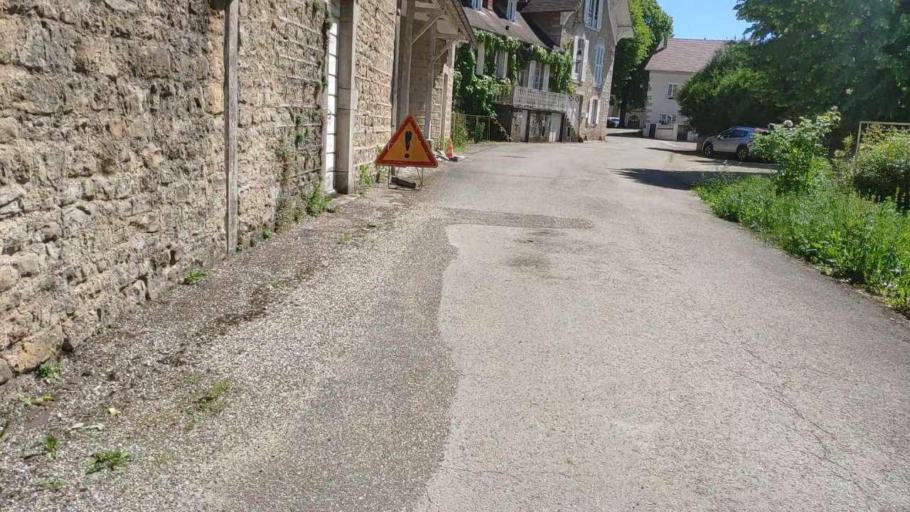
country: FR
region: Franche-Comte
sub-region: Departement du Jura
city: Perrigny
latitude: 46.7557
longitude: 5.6131
